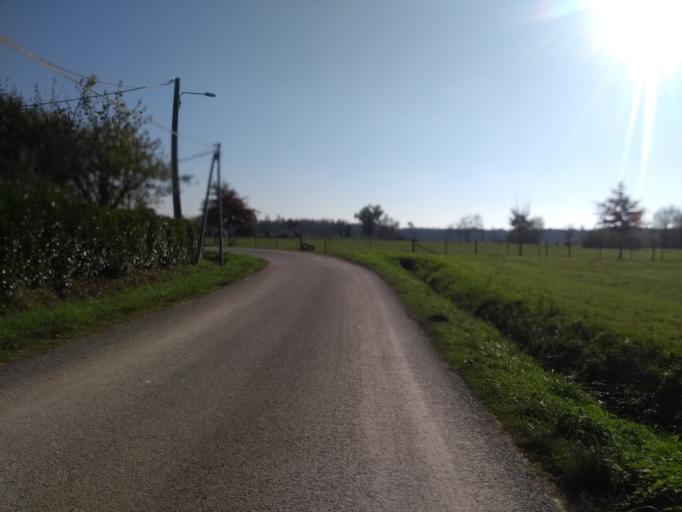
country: FR
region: Aquitaine
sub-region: Departement de la Gironde
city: Cambes
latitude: 44.7237
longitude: -0.4617
